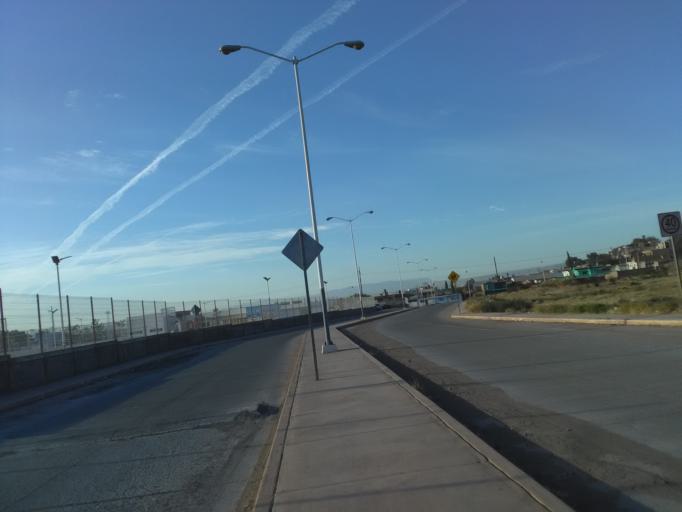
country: MX
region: Durango
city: Victoria de Durango
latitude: 24.0483
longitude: -104.6633
